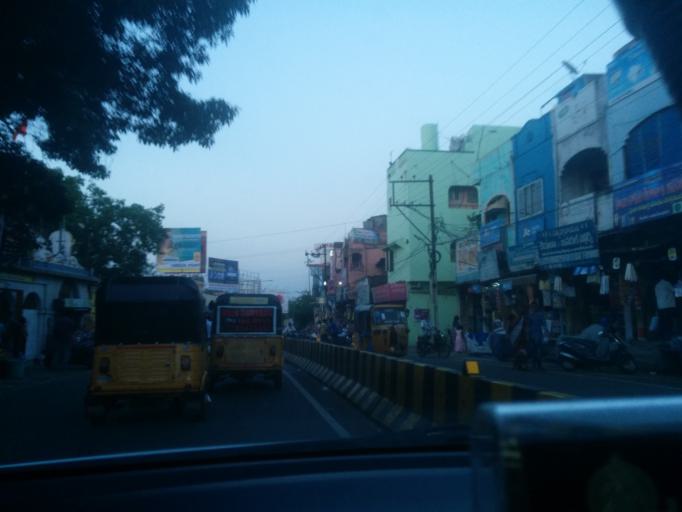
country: IN
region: Andhra Pradesh
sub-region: East Godavari
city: Rajahmundry
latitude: 17.0105
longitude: 81.7770
